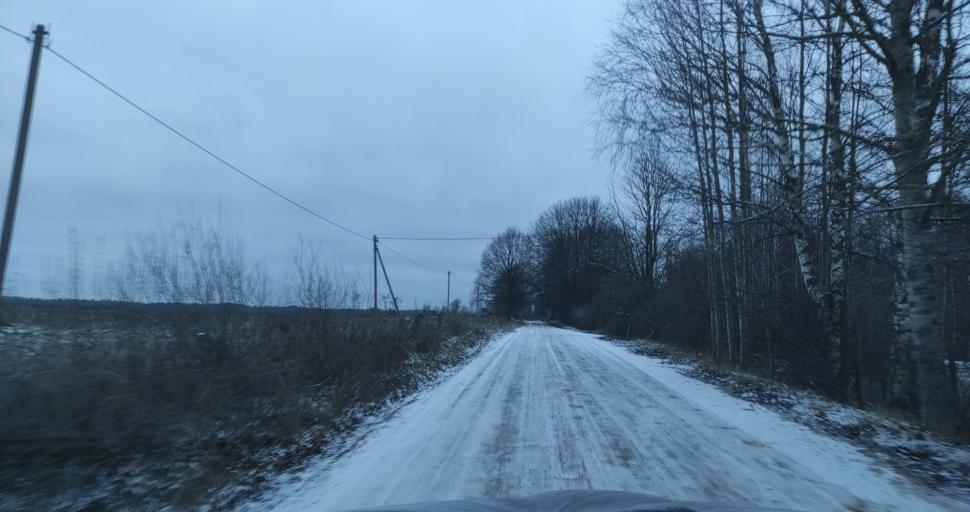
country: LV
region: Kuldigas Rajons
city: Kuldiga
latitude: 56.9690
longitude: 22.0631
